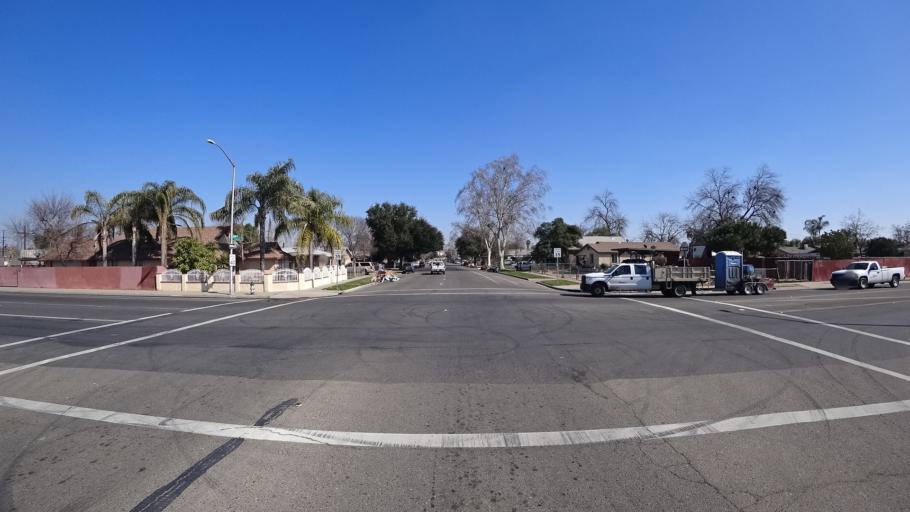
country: US
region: California
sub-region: Fresno County
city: Fresno
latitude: 36.7349
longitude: -119.8131
